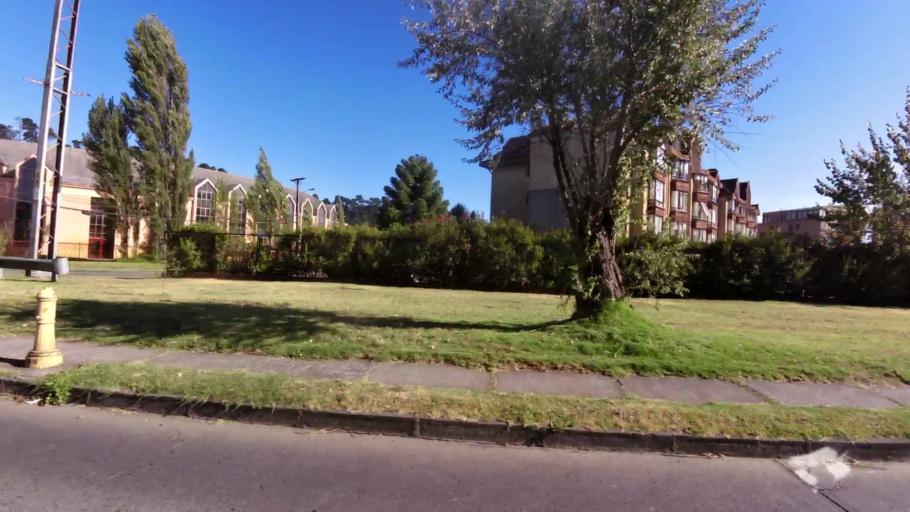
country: CL
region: Biobio
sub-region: Provincia de Concepcion
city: Concepcion
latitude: -36.8432
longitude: -73.1131
